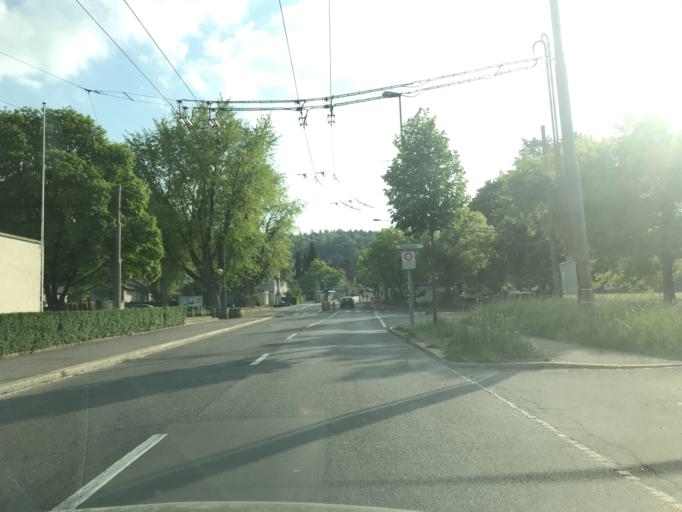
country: CH
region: Zurich
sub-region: Bezirk Winterthur
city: Mattenbach (Kreis 7) / Deutweg
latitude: 47.4921
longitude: 8.7362
